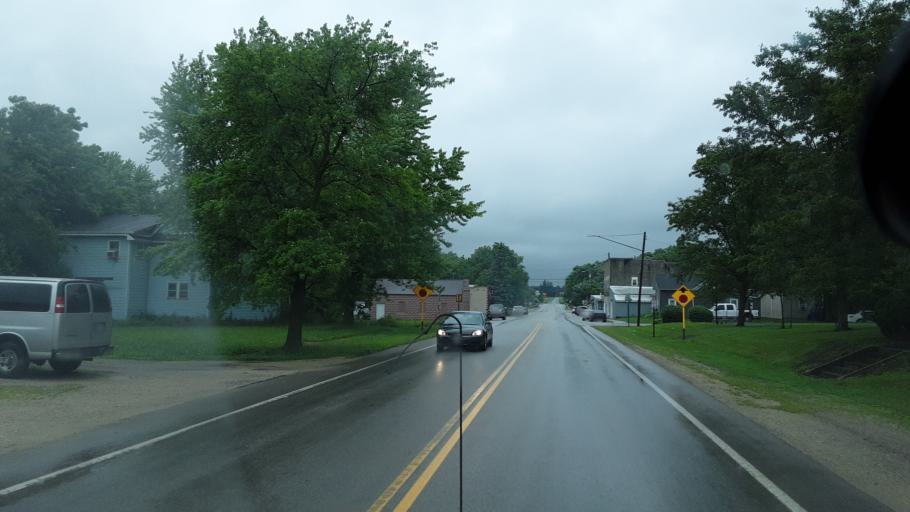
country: US
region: Ohio
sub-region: Mercer County
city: Rockford
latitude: 40.7482
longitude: -84.7927
